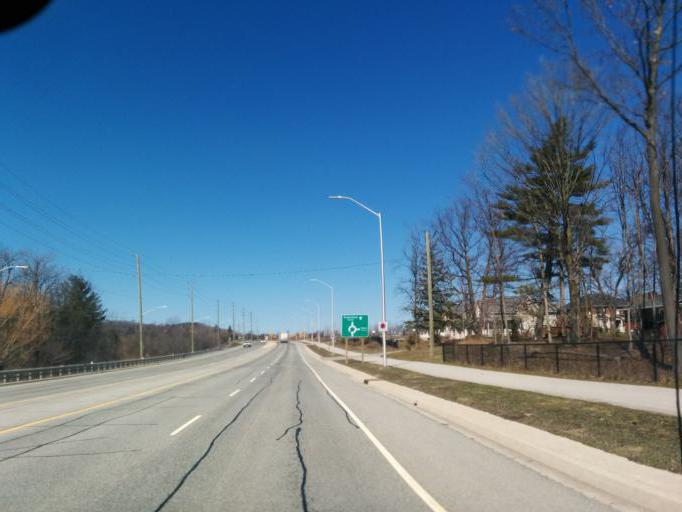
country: CA
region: Ontario
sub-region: Halton
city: Milton
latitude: 43.4934
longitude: -79.8943
